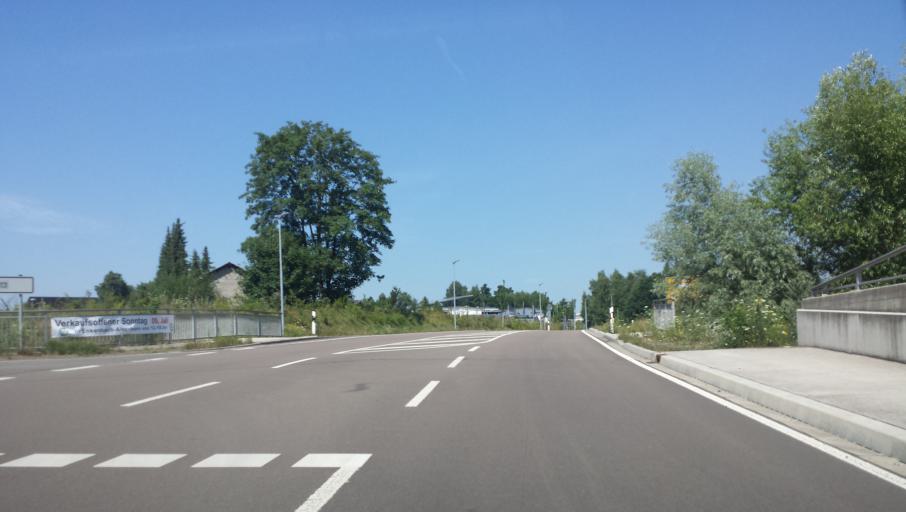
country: DE
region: Rheinland-Pfalz
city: Enkenbach-Alsenborn
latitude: 49.4919
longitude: 7.8983
